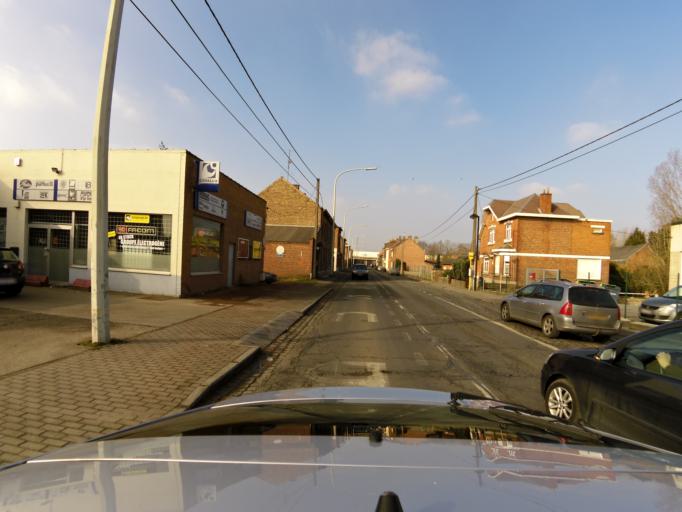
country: BE
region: Wallonia
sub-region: Province du Hainaut
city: Mons
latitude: 50.4646
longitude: 3.9344
